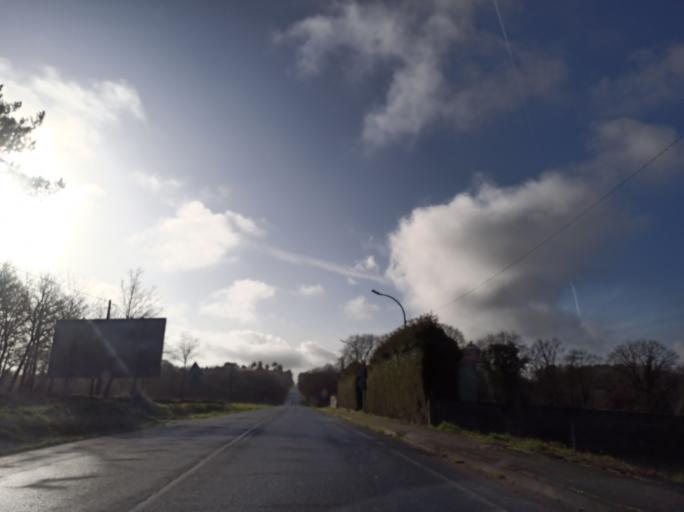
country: ES
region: Galicia
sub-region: Provincia da Coruna
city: Curtis
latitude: 43.1332
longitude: -8.0341
